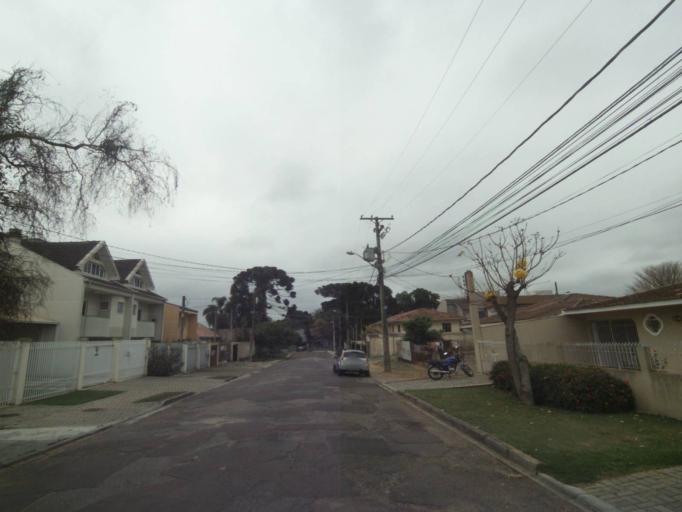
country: BR
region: Parana
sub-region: Pinhais
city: Pinhais
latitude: -25.4794
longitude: -49.2287
